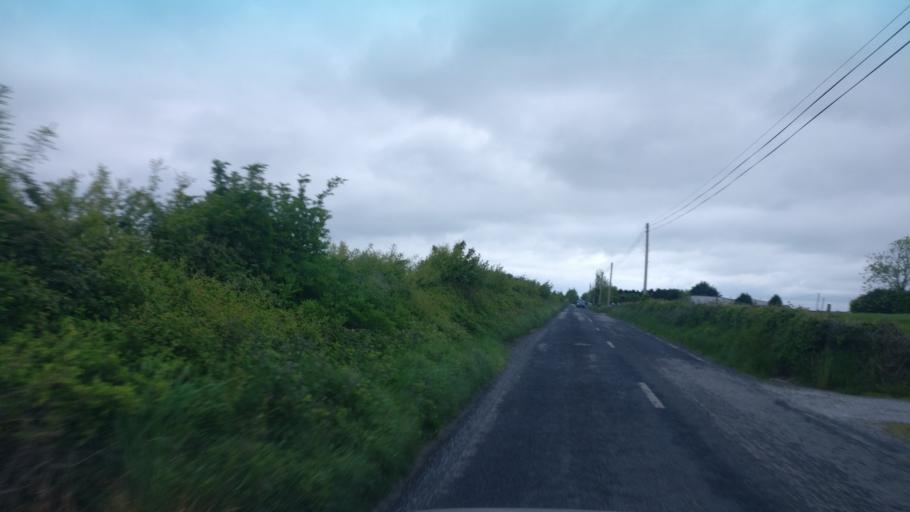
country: IE
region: Connaught
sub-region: County Galway
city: Portumna
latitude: 53.1112
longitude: -8.2738
